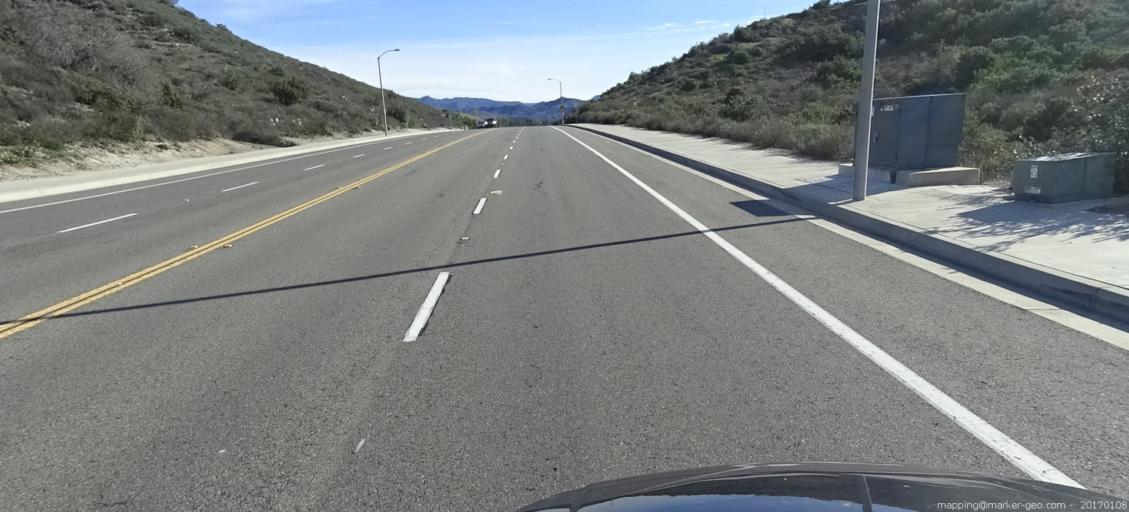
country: US
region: California
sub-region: Orange County
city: Coto De Caza
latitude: 33.5895
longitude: -117.6037
